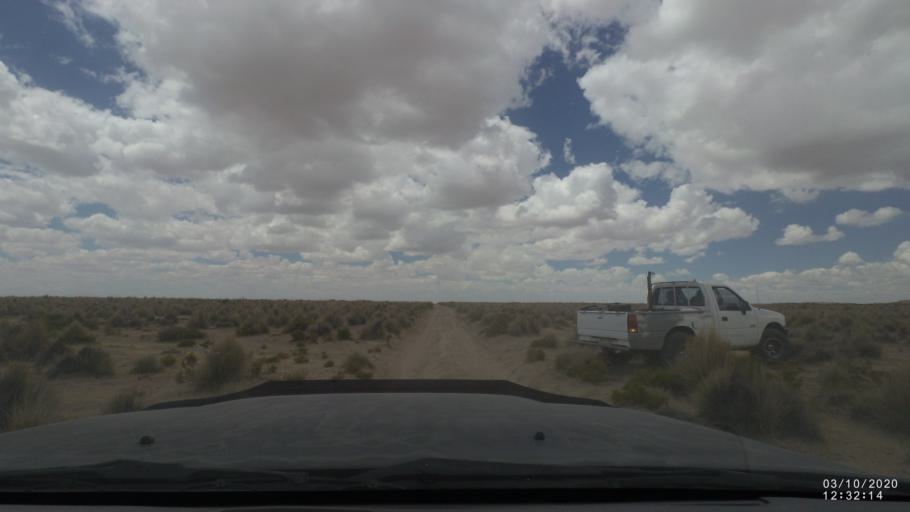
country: BO
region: Oruro
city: Poopo
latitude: -18.6872
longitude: -67.5356
